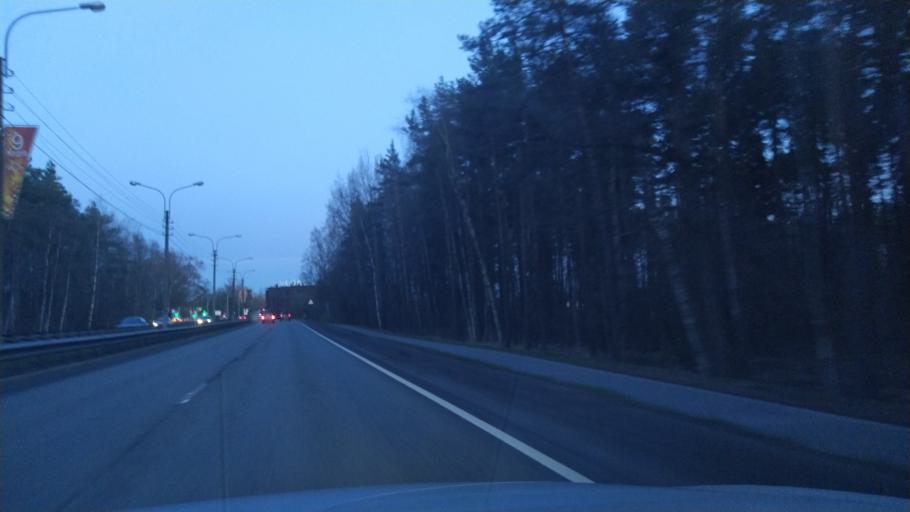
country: RU
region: St.-Petersburg
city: Tarkhovka
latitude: 60.0614
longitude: 29.9726
